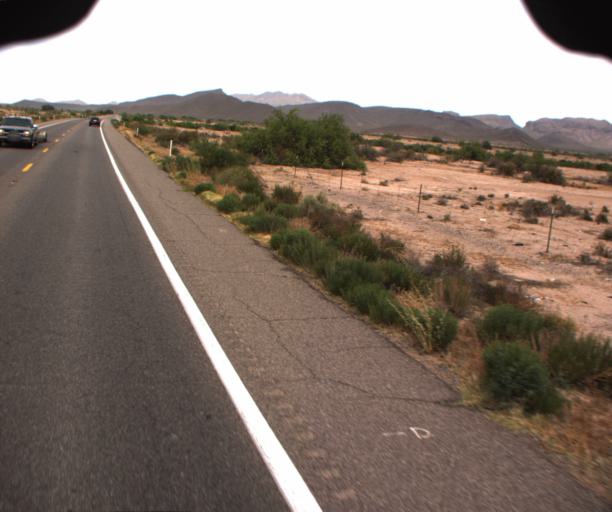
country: US
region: Arizona
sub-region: Pinal County
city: Sacaton
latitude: 33.0818
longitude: -111.7053
